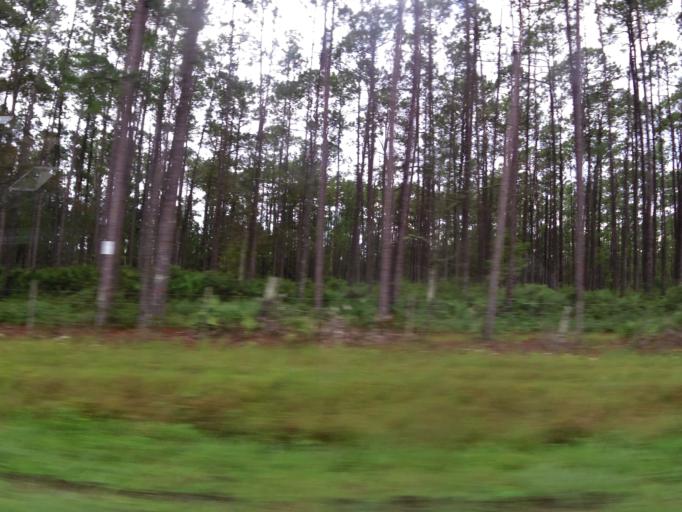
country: US
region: Florida
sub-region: Duval County
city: Baldwin
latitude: 30.4003
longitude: -81.9886
